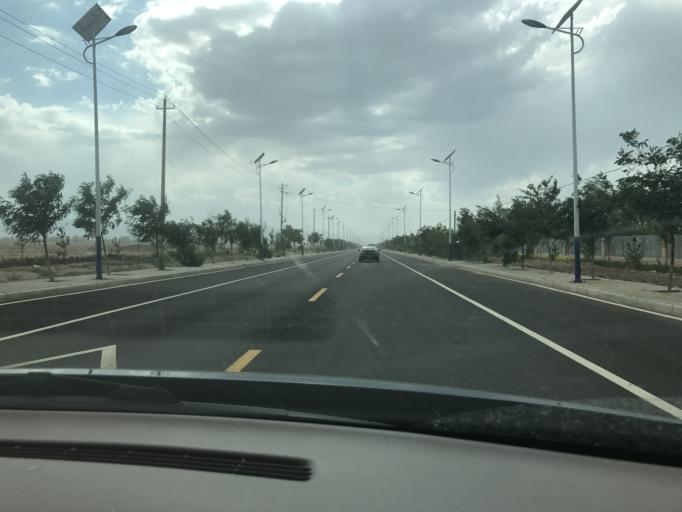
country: CN
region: Gansu Sheng
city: Wuwei
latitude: 38.1031
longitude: 102.4528
